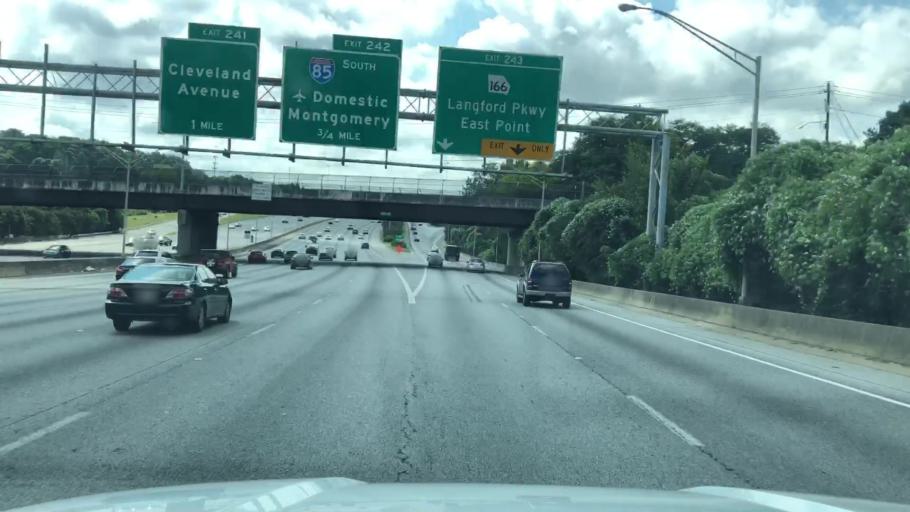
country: US
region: Georgia
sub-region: Fulton County
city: East Point
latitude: 33.7040
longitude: -84.4042
